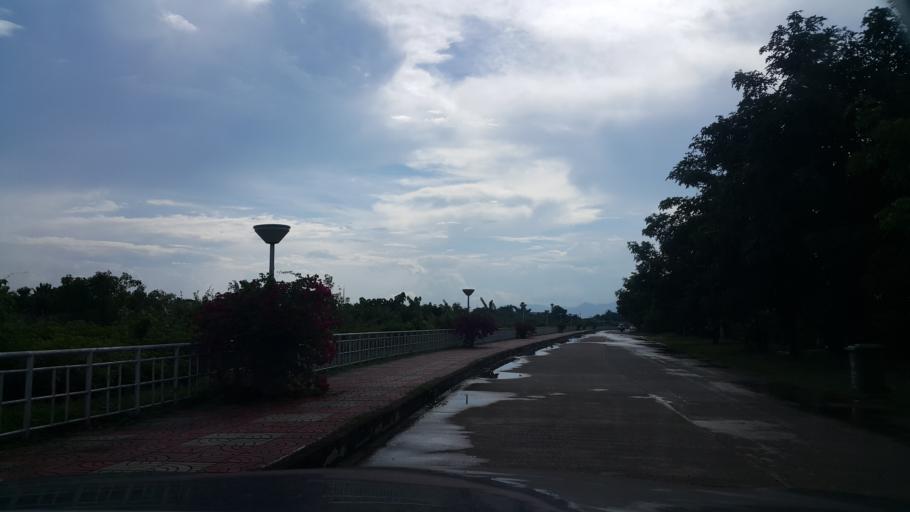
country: TH
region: Lampang
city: Thoen
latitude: 17.6162
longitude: 99.2257
